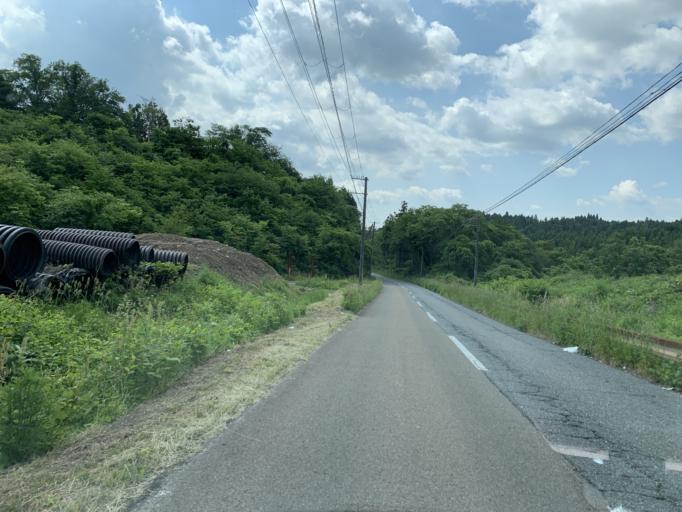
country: JP
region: Miyagi
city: Furukawa
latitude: 38.7757
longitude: 140.9602
